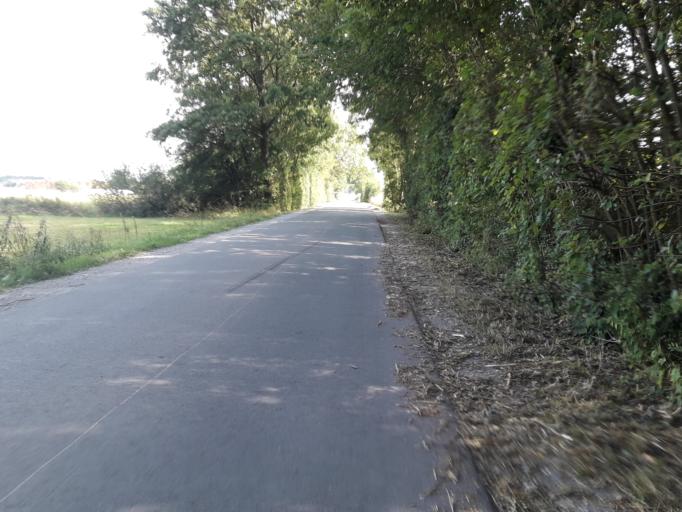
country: DE
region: North Rhine-Westphalia
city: Bad Lippspringe
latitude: 51.7429
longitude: 8.7952
